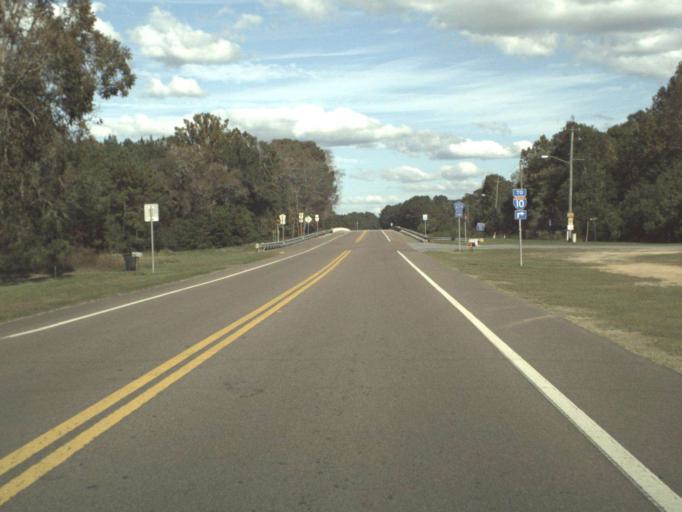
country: US
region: Florida
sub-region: Holmes County
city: Bonifay
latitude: 30.7737
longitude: -85.8131
